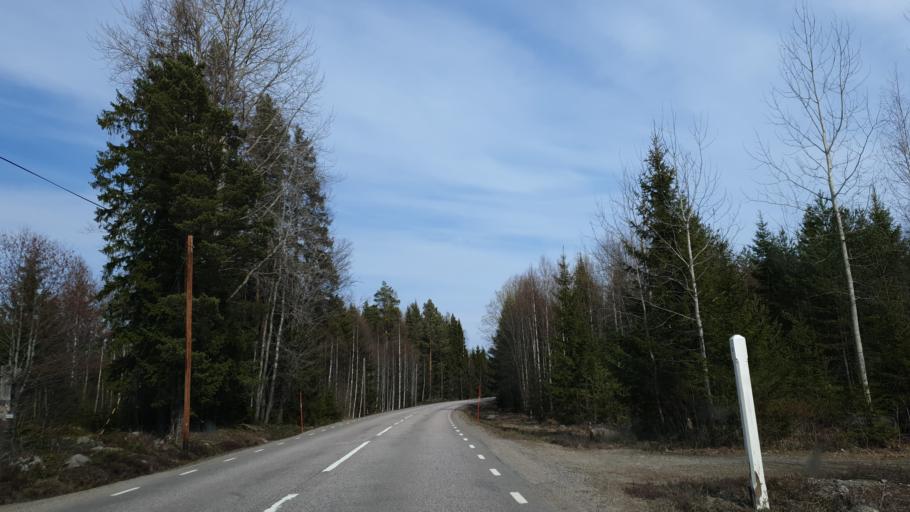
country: SE
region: Gaevleborg
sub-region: Gavle Kommun
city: Norrsundet
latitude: 60.9804
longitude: 17.0635
